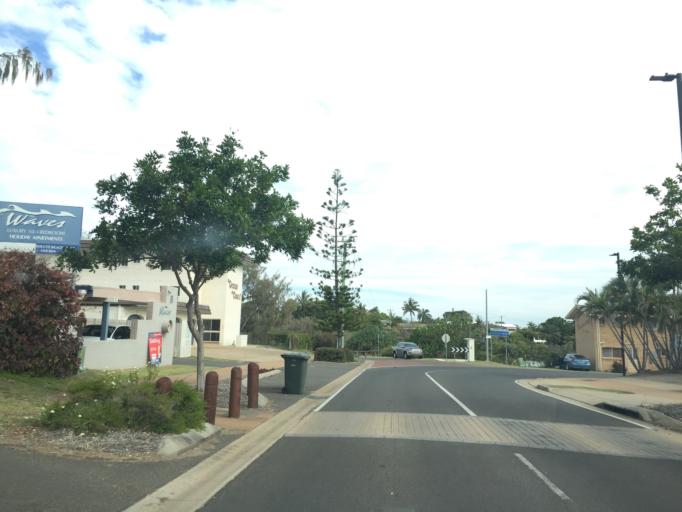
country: AU
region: Queensland
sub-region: Bundaberg
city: Bundaberg
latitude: -24.8248
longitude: 152.4652
